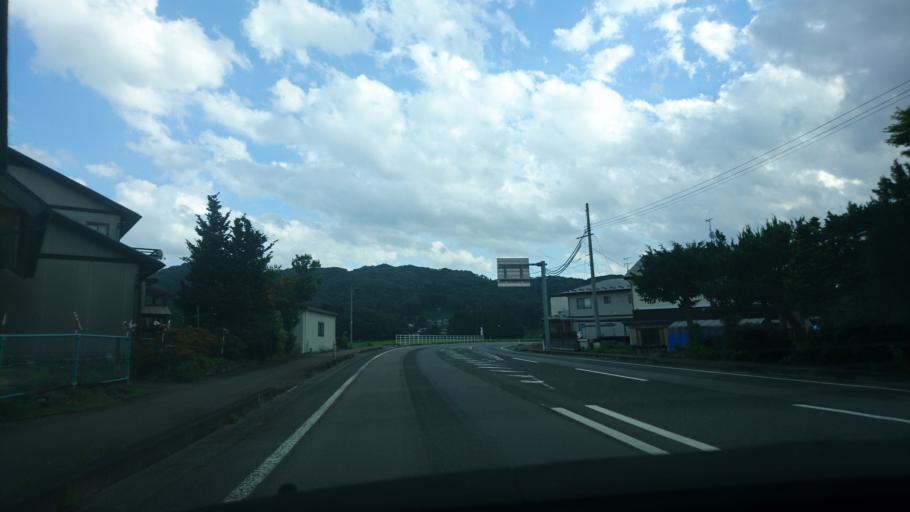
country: JP
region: Iwate
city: Kitakami
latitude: 39.2835
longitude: 141.1370
